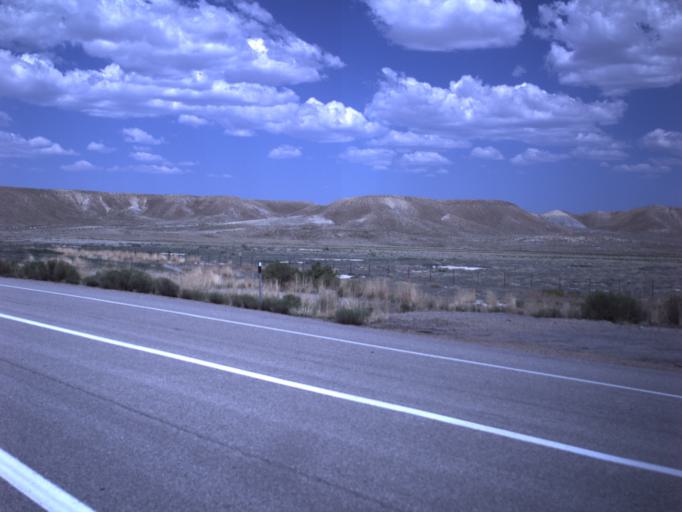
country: US
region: Utah
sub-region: Carbon County
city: Price
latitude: 39.4583
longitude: -110.8604
